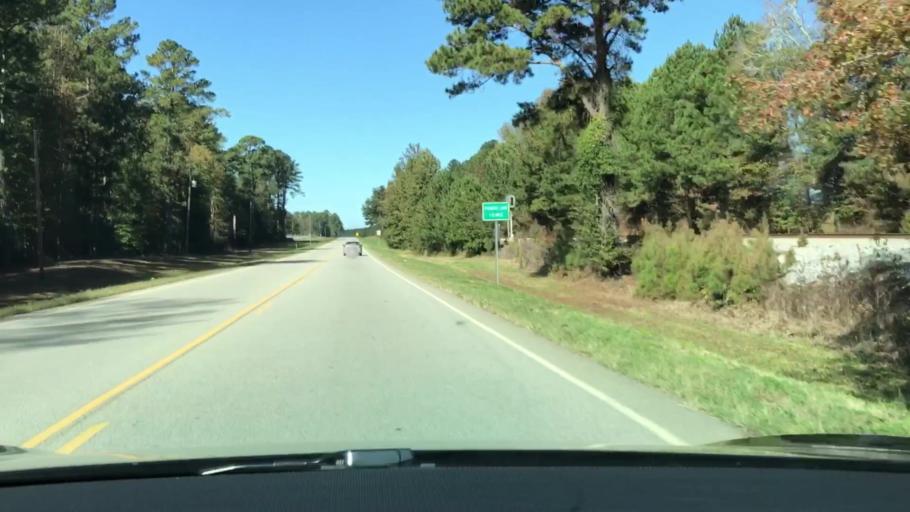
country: US
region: Georgia
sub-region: Warren County
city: Firing Range
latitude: 33.4713
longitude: -82.7217
